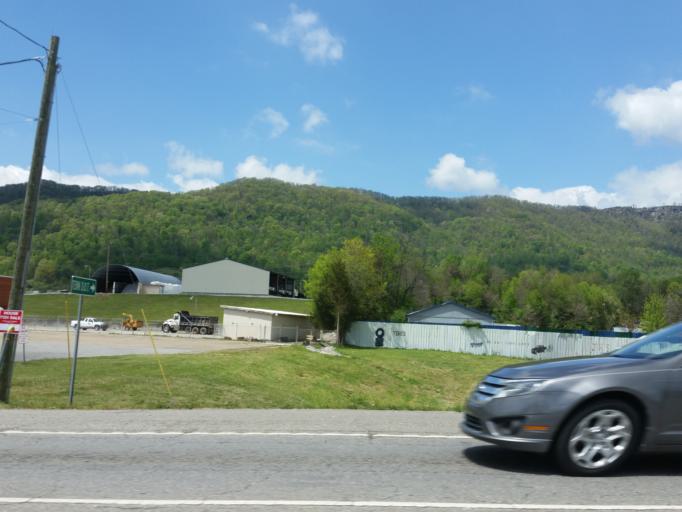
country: US
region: Tennessee
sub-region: Campbell County
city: Fincastle
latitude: 36.4071
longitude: -84.0636
